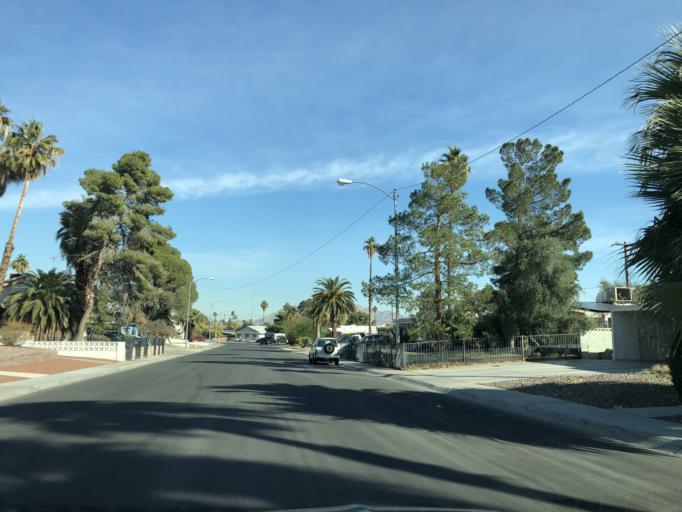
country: US
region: Nevada
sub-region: Clark County
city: Winchester
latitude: 36.1280
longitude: -115.1320
